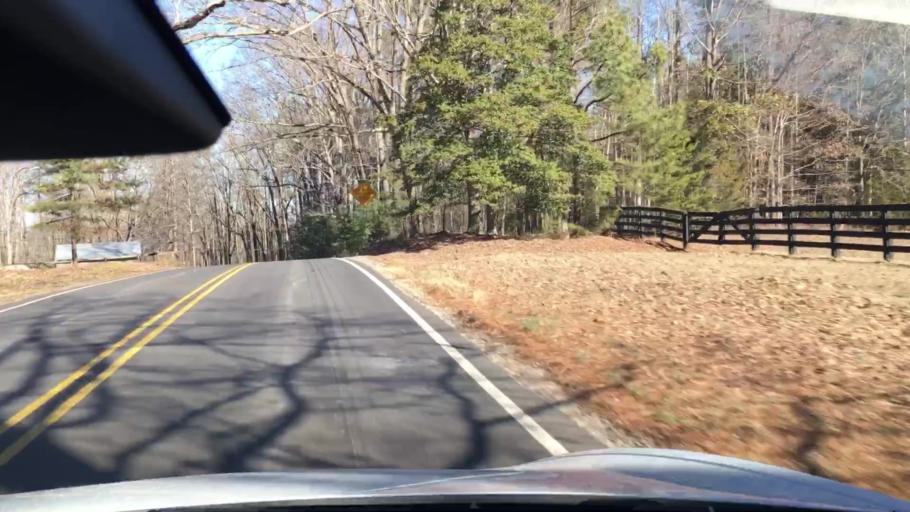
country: US
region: Virginia
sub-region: Powhatan County
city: Powhatan
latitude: 37.5774
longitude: -77.7731
